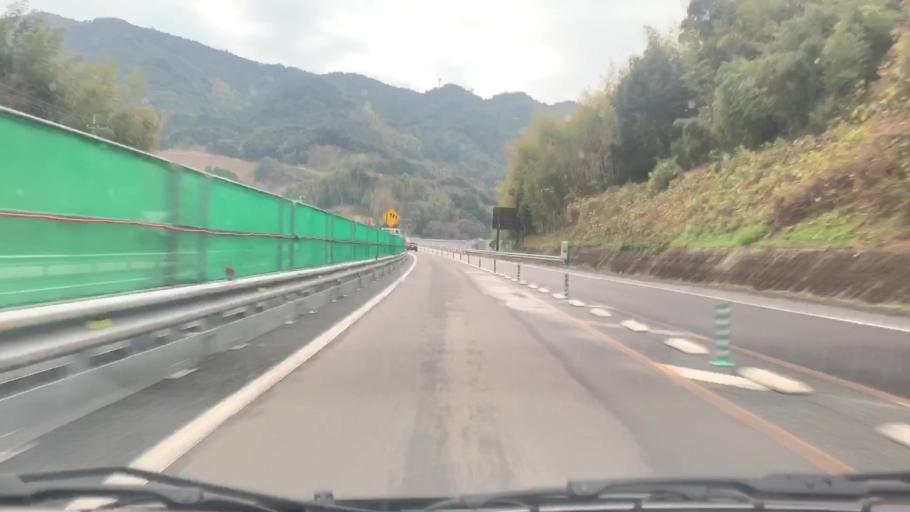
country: JP
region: Nagasaki
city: Obita
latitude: 32.8025
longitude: 129.9655
